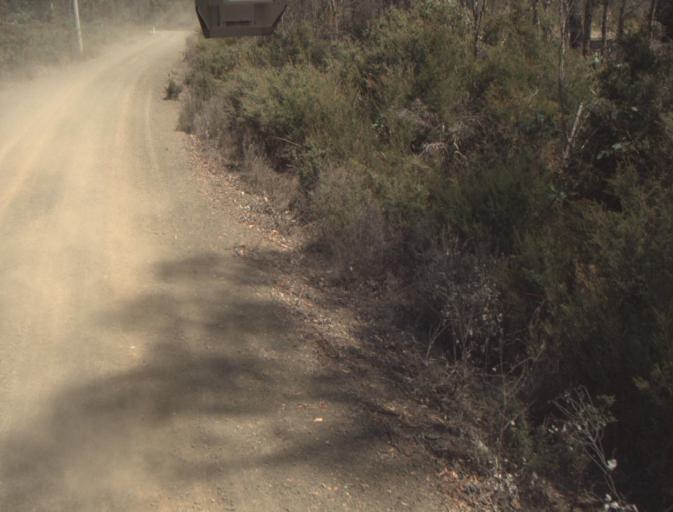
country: AU
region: Tasmania
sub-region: Launceston
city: Mayfield
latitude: -41.2786
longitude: 147.0972
